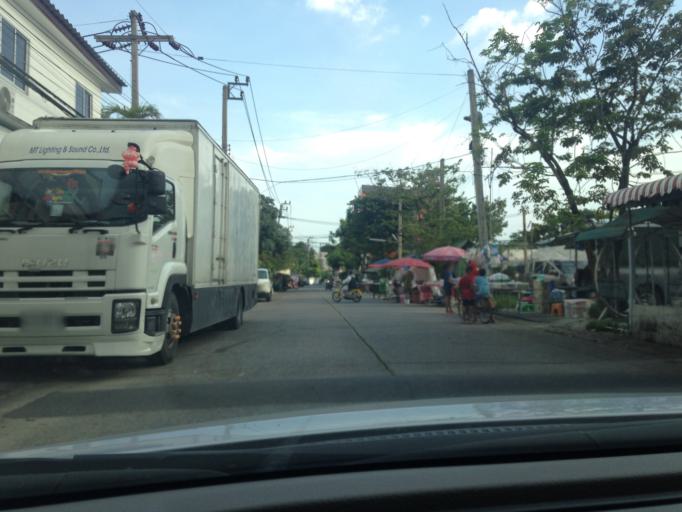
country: TH
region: Bangkok
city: Khan Na Yao
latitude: 13.8382
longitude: 100.6438
